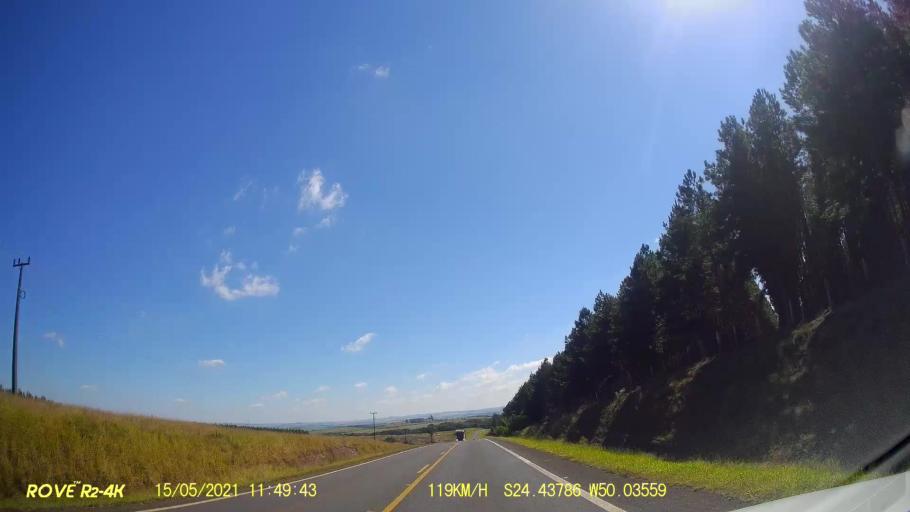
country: BR
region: Parana
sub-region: Pirai Do Sul
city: Pirai do Sul
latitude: -24.4395
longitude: -50.0339
